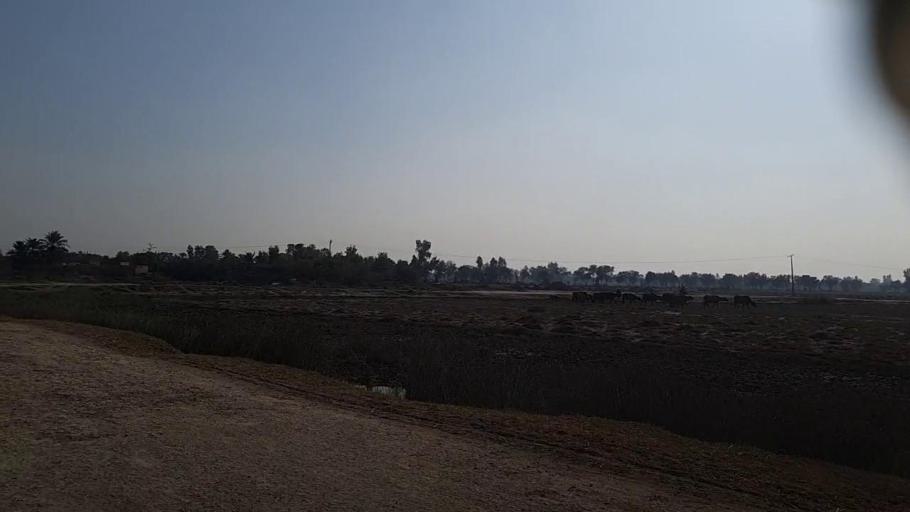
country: PK
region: Sindh
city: Mirpur Mathelo
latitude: 27.8913
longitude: 69.6047
